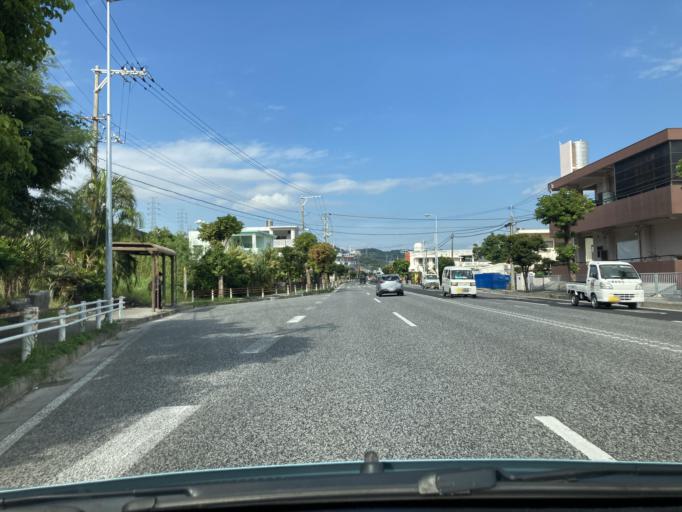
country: JP
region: Okinawa
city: Ginowan
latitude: 26.2592
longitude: 127.7865
